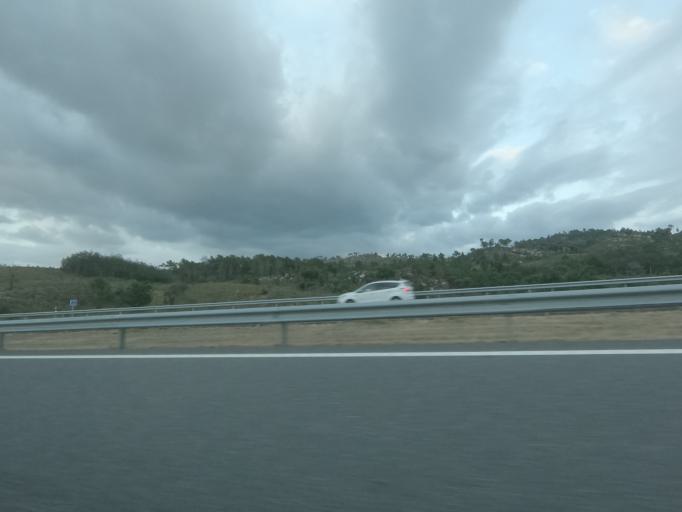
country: ES
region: Galicia
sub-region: Provincia de Ourense
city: Carballeda de Avia
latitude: 42.3000
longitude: -8.1814
